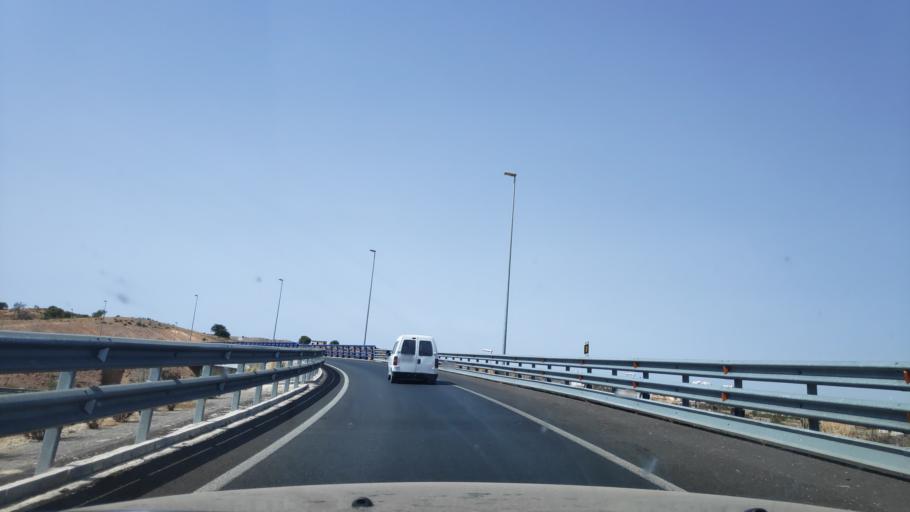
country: ES
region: Murcia
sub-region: Murcia
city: Murcia
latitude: 38.0306
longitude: -1.1528
